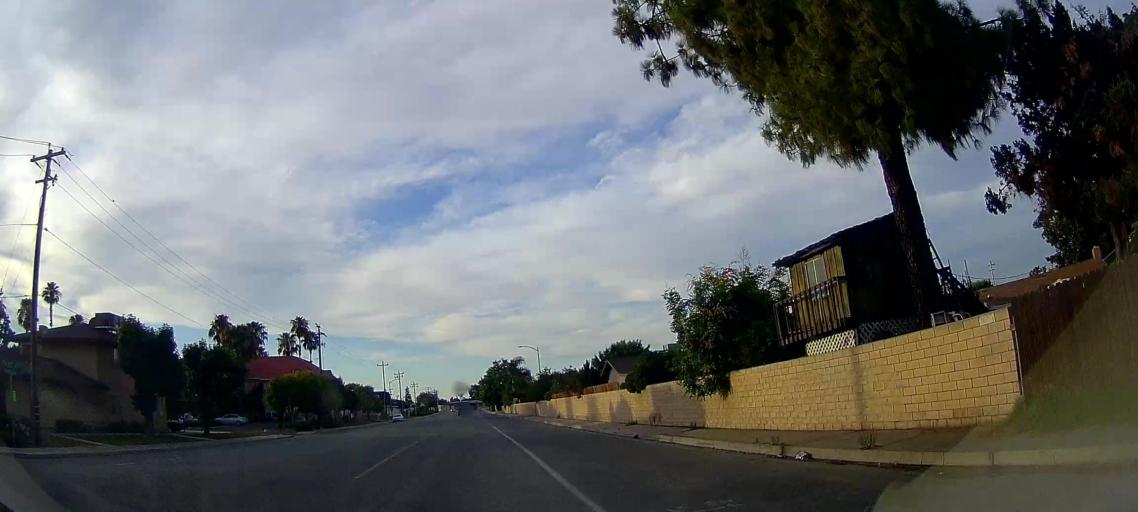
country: US
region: California
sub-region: Kern County
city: Bakersfield
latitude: 35.3360
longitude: -119.0477
